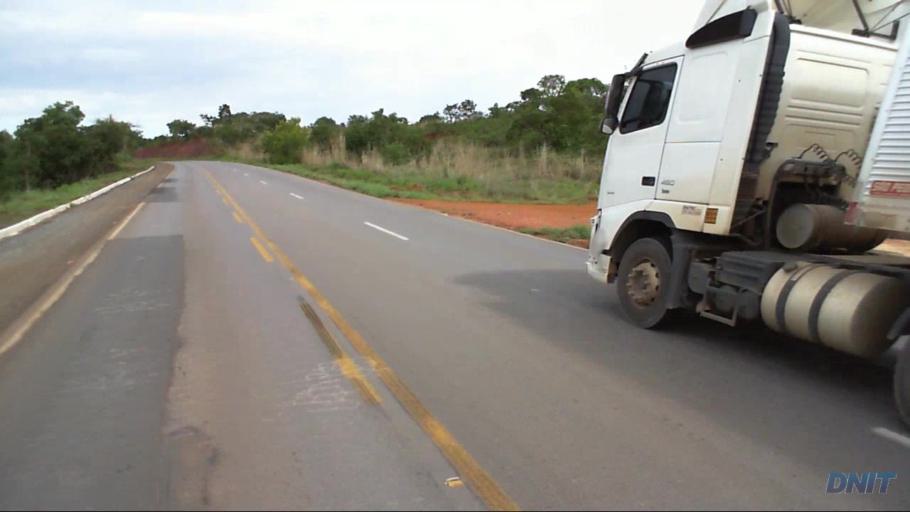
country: BR
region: Goias
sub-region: Barro Alto
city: Barro Alto
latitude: -14.8697
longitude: -49.0072
